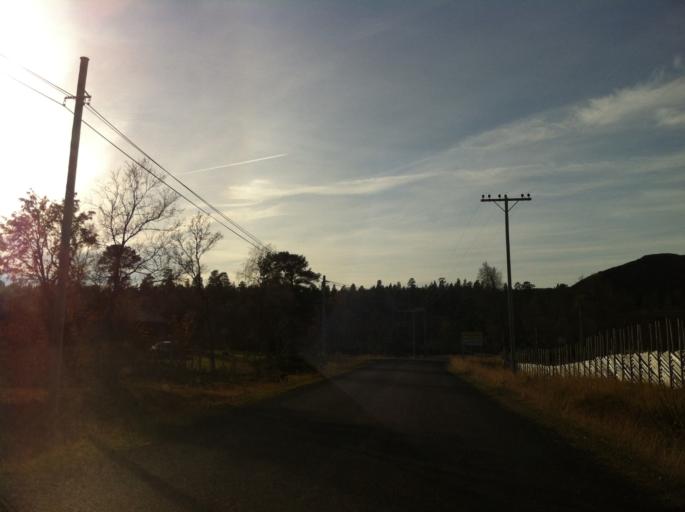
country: NO
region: Hedmark
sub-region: Engerdal
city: Engerdal
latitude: 62.0835
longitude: 12.0916
